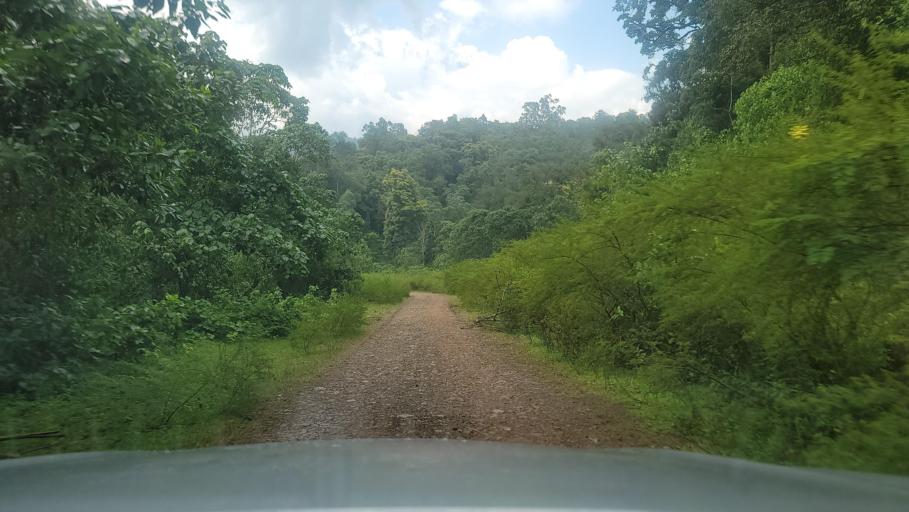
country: ET
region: Southern Nations, Nationalities, and People's Region
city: Bonga
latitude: 7.6372
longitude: 36.2287
